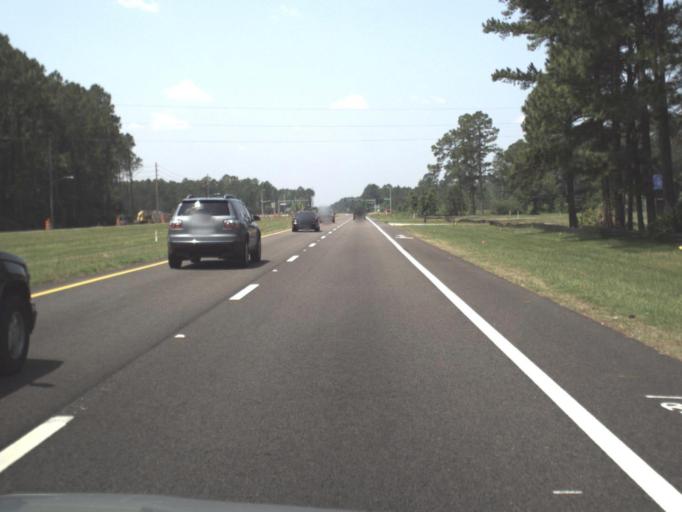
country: US
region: Florida
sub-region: Duval County
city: Baldwin
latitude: 30.2632
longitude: -81.8581
